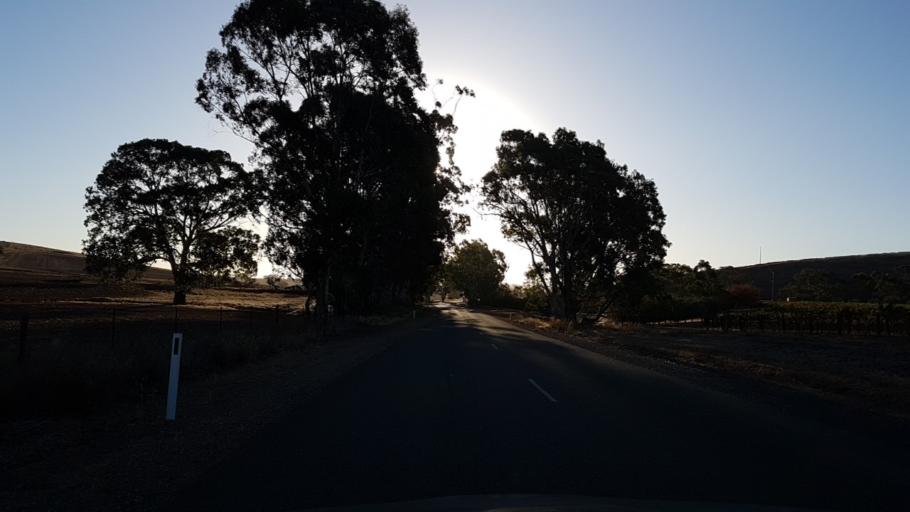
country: AU
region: South Australia
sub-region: Clare and Gilbert Valleys
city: Clare
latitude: -34.0014
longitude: 138.7518
